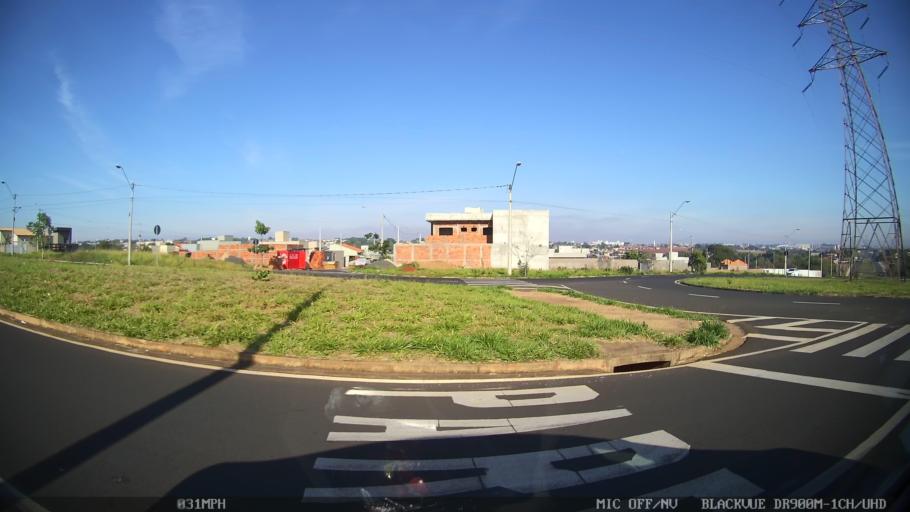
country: BR
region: Sao Paulo
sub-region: Sao Jose Do Rio Preto
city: Sao Jose do Rio Preto
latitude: -20.7655
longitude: -49.3580
